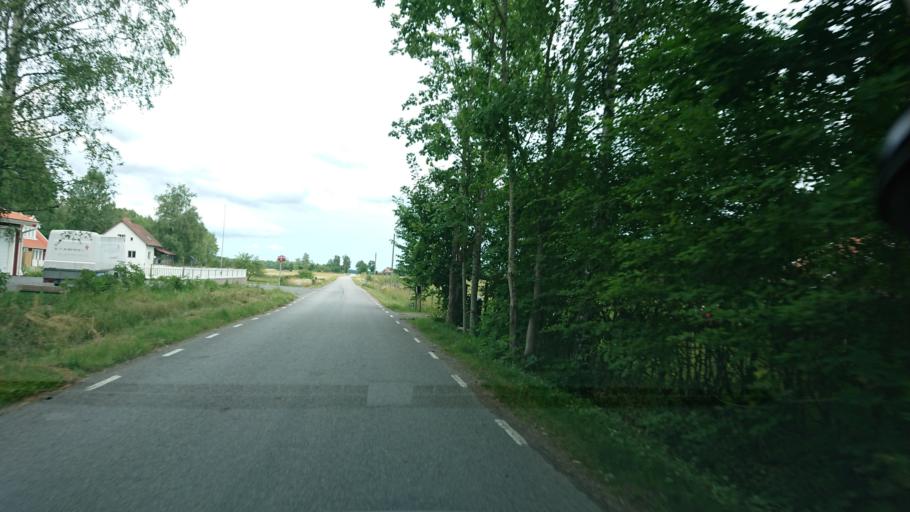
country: SE
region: Uppsala
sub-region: Osthammars Kommun
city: Bjorklinge
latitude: 59.9991
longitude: 17.4756
